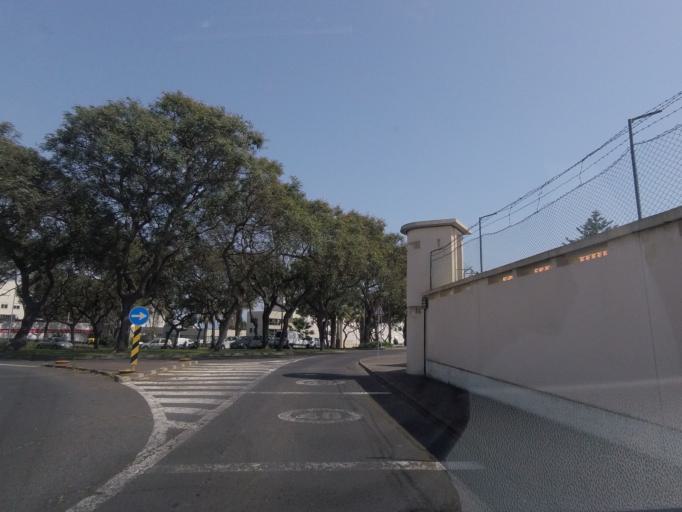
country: PT
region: Madeira
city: Camara de Lobos
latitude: 32.6437
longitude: -16.9351
